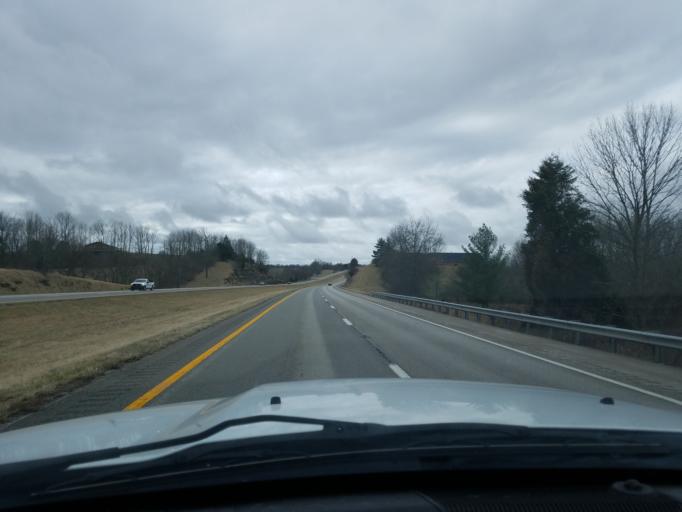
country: US
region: Kentucky
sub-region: Clark County
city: Winchester
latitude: 38.0296
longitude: -84.0911
